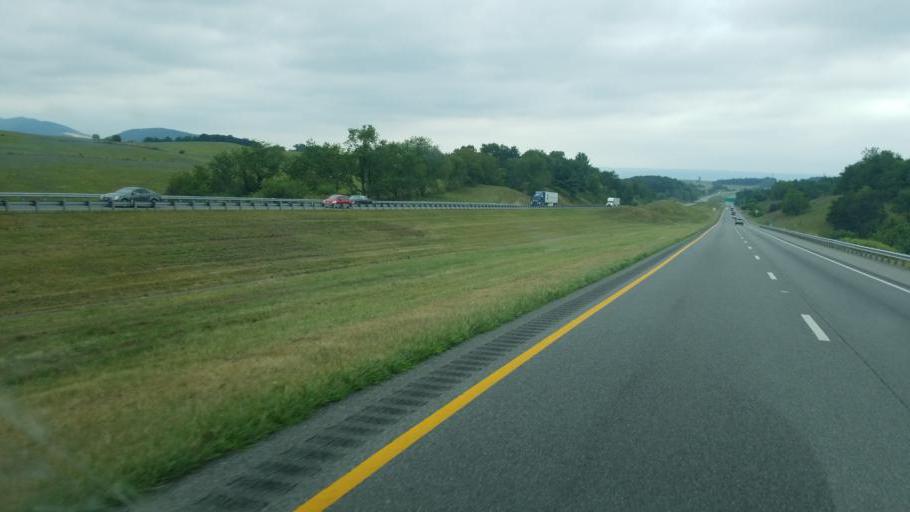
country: US
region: Virginia
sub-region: Pulaski County
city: Pulaski
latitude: 36.9190
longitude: -80.8982
